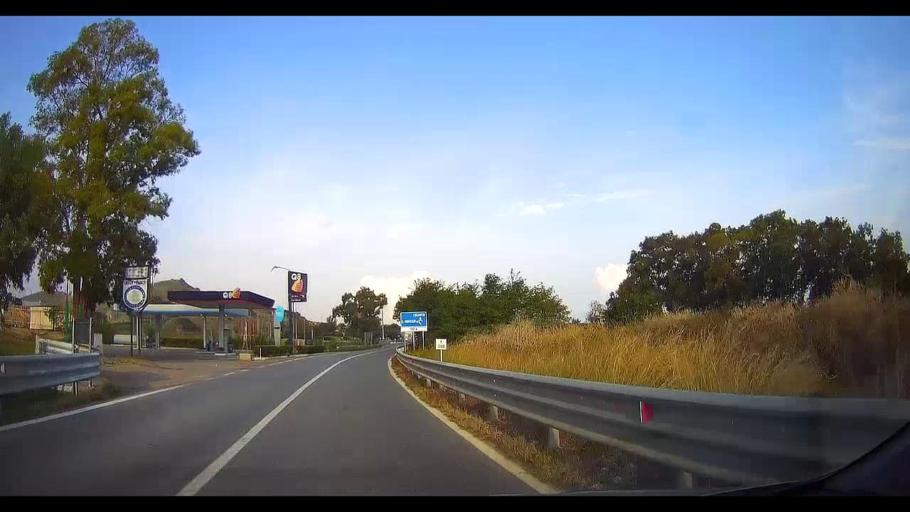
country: IT
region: Calabria
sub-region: Provincia di Cosenza
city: Cariati
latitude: 39.5163
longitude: 16.9125
